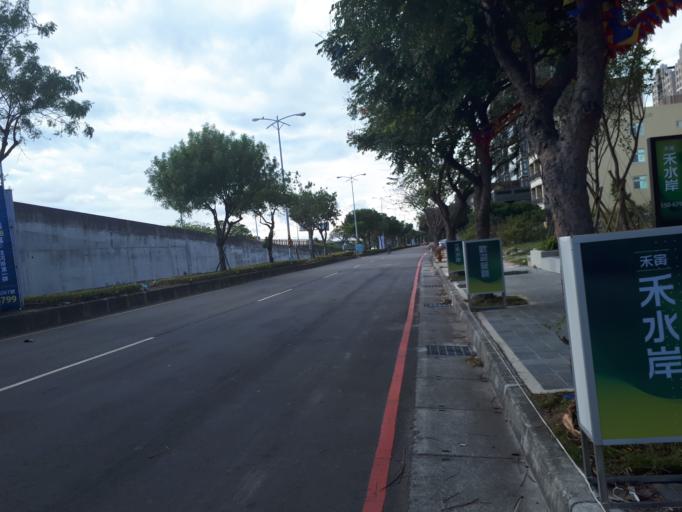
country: TW
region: Taiwan
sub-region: Hsinchu
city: Zhubei
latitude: 24.8002
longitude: 121.0370
